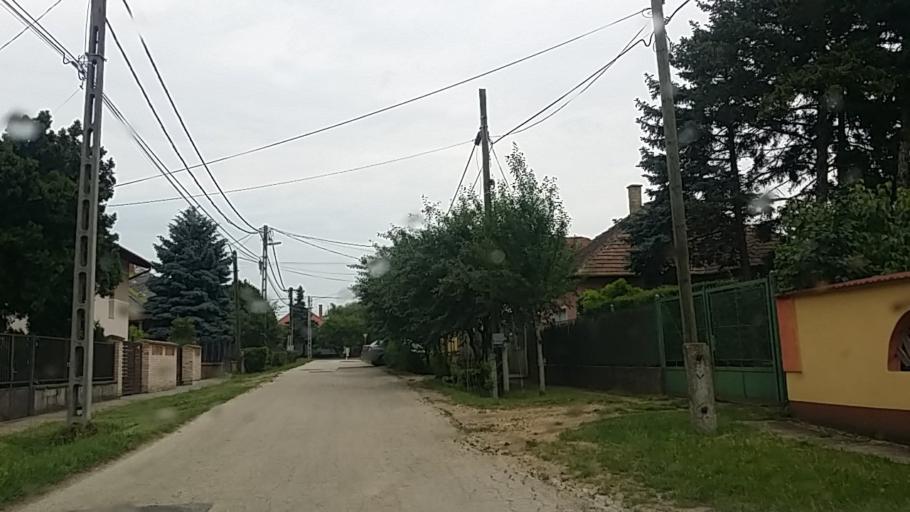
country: HU
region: Pest
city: Vecses
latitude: 47.4022
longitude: 19.2617
